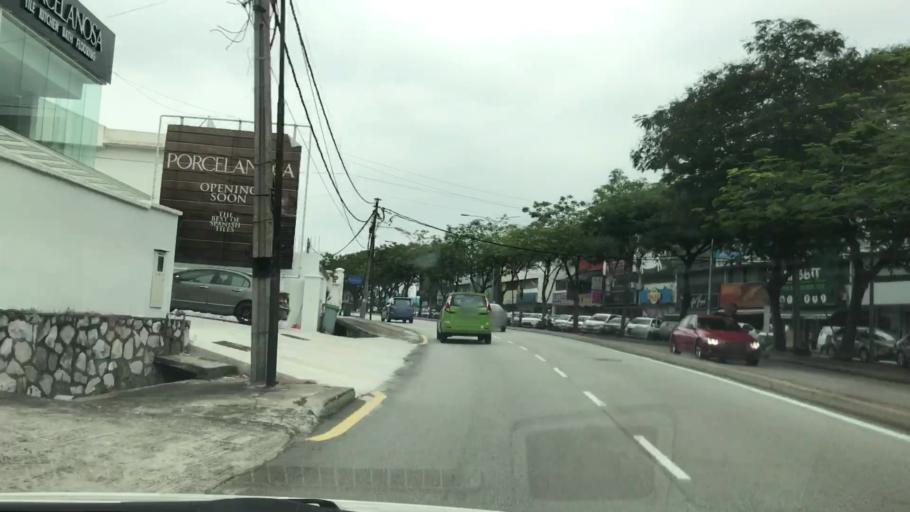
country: MY
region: Selangor
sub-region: Petaling
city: Petaling Jaya
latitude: 3.1171
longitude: 101.6235
